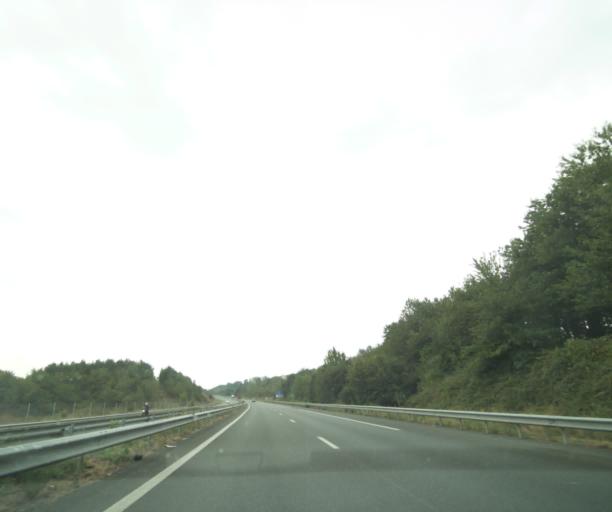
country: FR
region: Pays de la Loire
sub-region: Departement de la Vendee
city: Bournezeau
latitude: 46.6614
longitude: -1.1567
